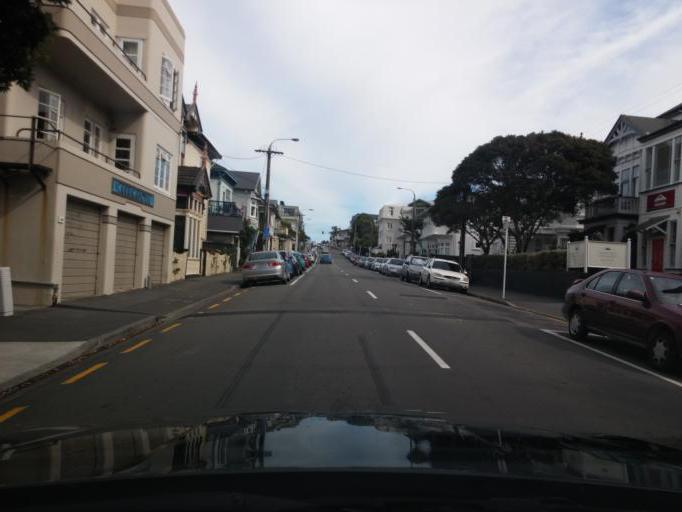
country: NZ
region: Wellington
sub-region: Wellington City
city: Wellington
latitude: -41.2864
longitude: 174.7732
